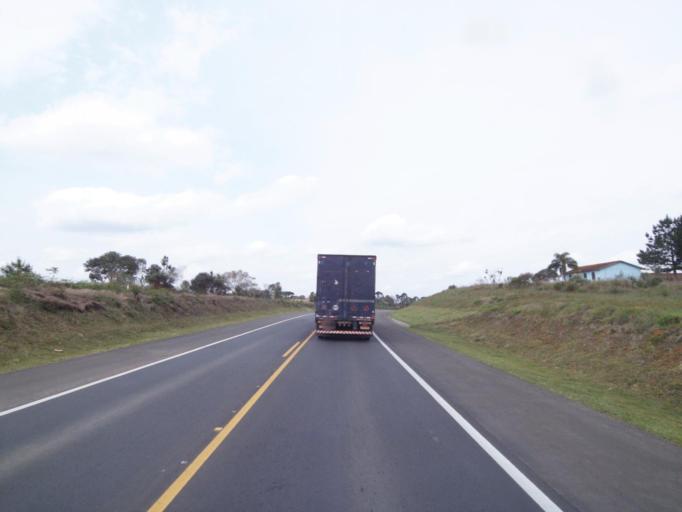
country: BR
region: Parana
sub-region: Irati
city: Irati
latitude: -25.4685
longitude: -50.4772
